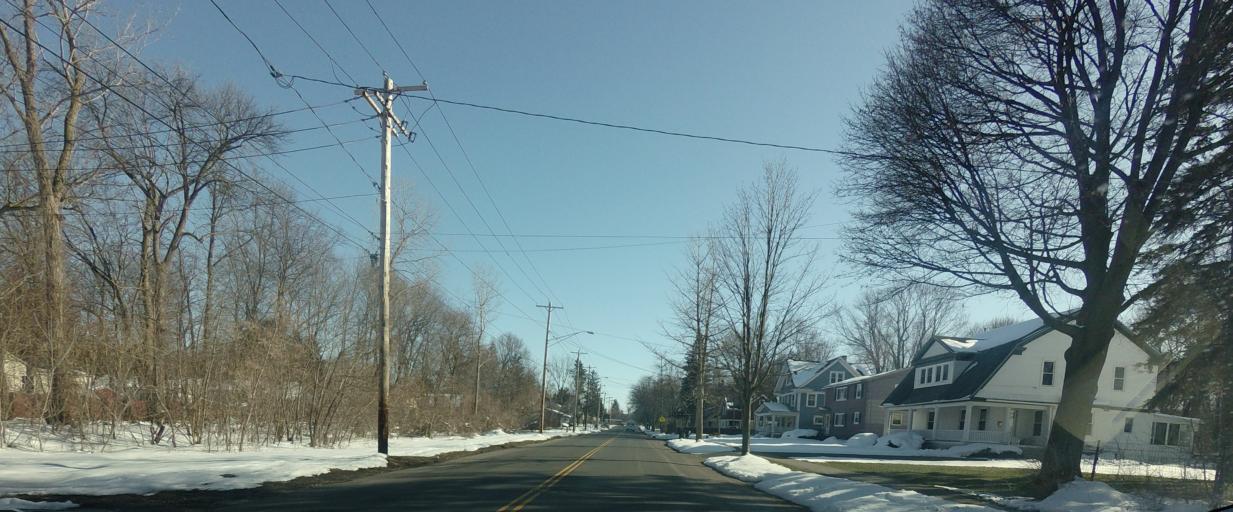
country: US
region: New York
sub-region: Onondaga County
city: Nedrow
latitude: 43.0077
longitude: -76.1475
